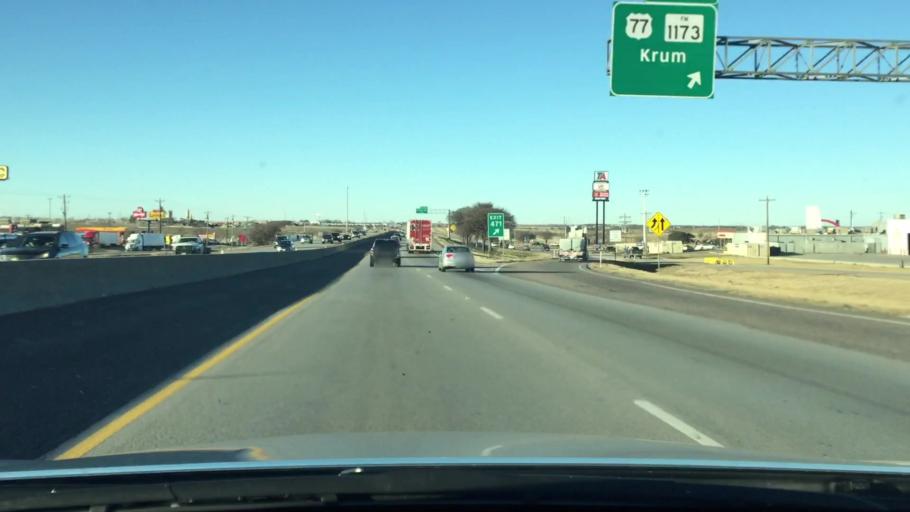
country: US
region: Texas
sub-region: Denton County
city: Krum
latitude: 33.2603
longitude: -97.1778
